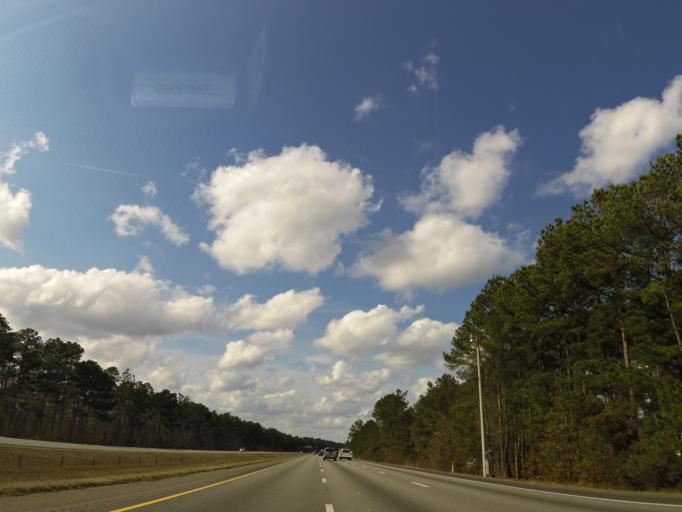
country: US
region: South Carolina
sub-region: Berkeley County
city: Sangaree
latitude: 33.0218
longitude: -80.1292
